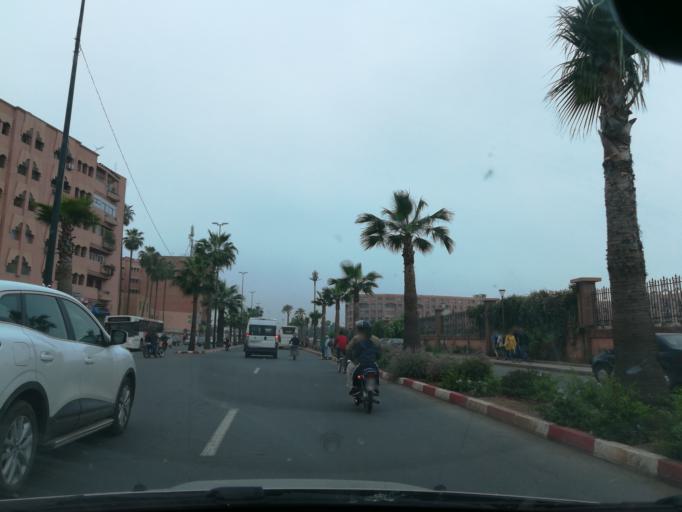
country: MA
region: Marrakech-Tensift-Al Haouz
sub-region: Marrakech
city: Marrakesh
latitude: 31.6393
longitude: -8.0000
